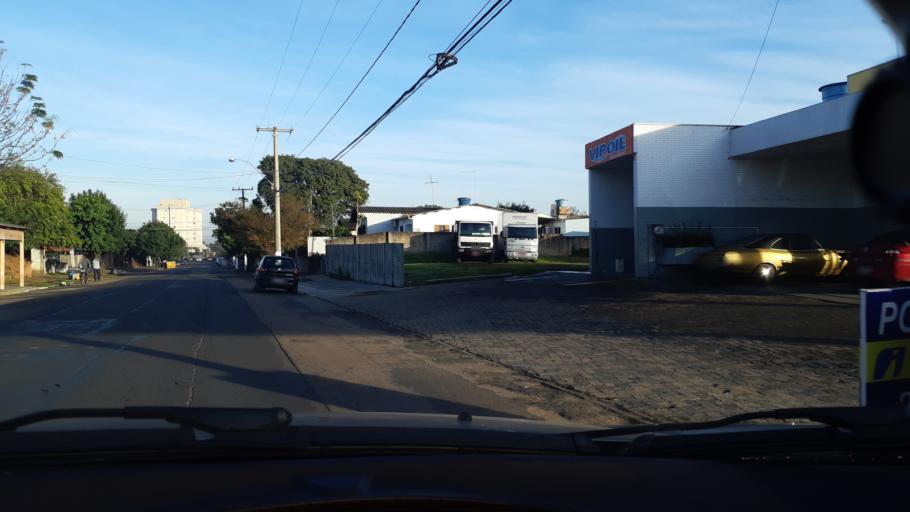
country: BR
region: Rio Grande do Sul
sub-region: Sapucaia Do Sul
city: Sapucaia
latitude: -29.8442
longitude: -51.1533
